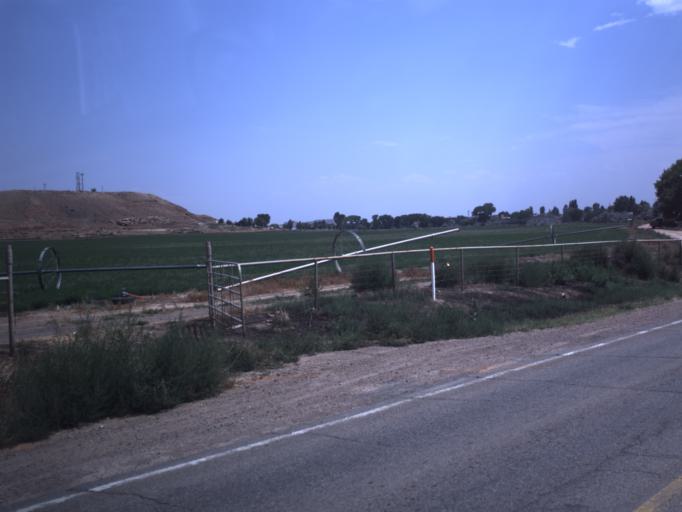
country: US
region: Utah
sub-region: Duchesne County
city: Roosevelt
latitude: 40.3149
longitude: -110.0126
